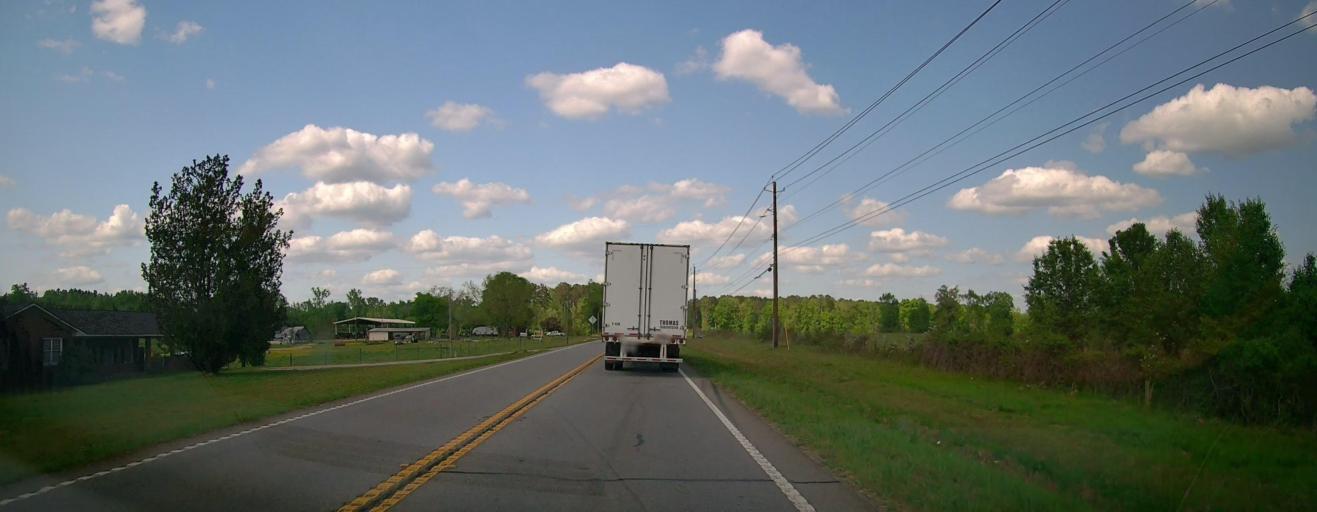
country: US
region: Georgia
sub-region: Greene County
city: Greensboro
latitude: 33.5131
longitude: -83.2266
